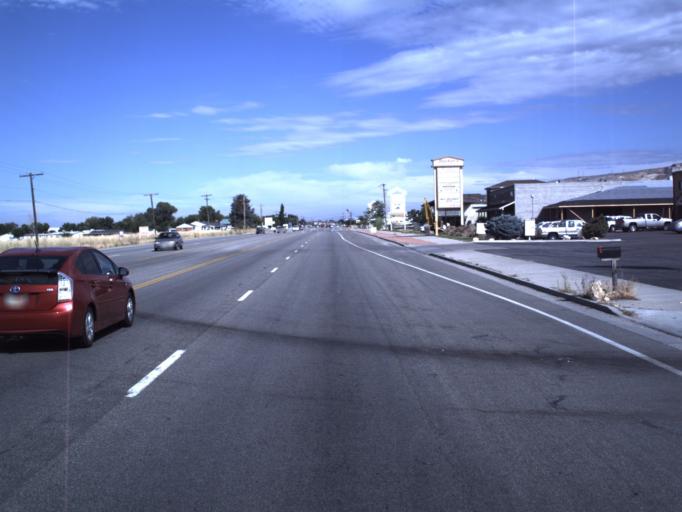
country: US
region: Utah
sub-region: Weber County
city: Harrisville
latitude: 41.2975
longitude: -111.9970
